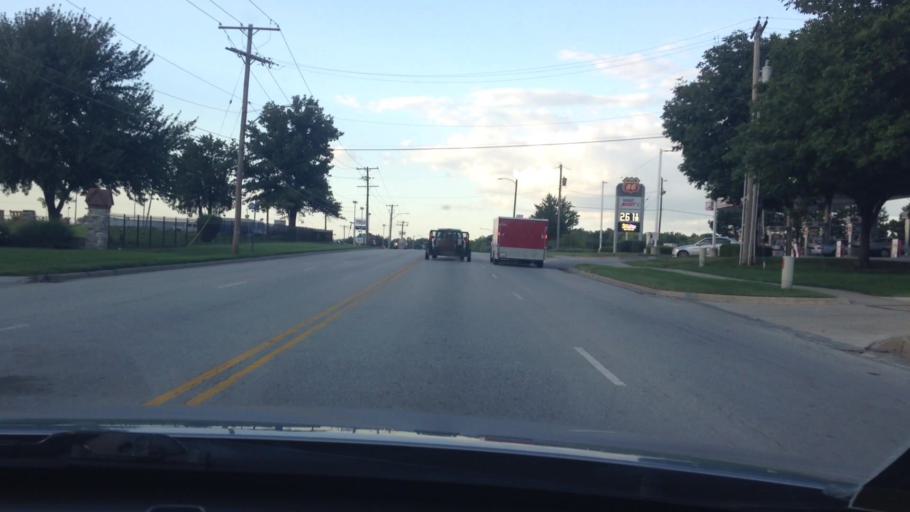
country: US
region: Missouri
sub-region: Jackson County
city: Raytown
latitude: 38.9976
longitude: -94.4825
